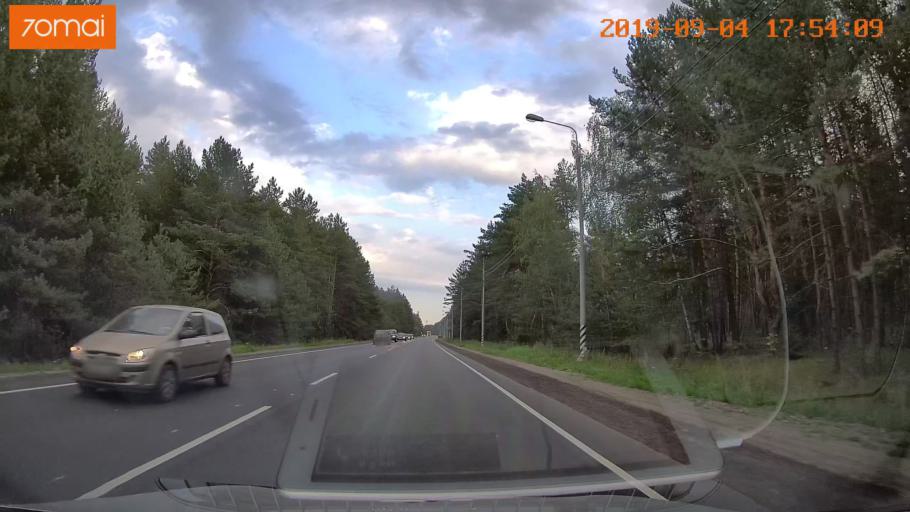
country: RU
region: Moskovskaya
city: Imeni Tsyurupy
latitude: 55.5122
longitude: 38.7375
